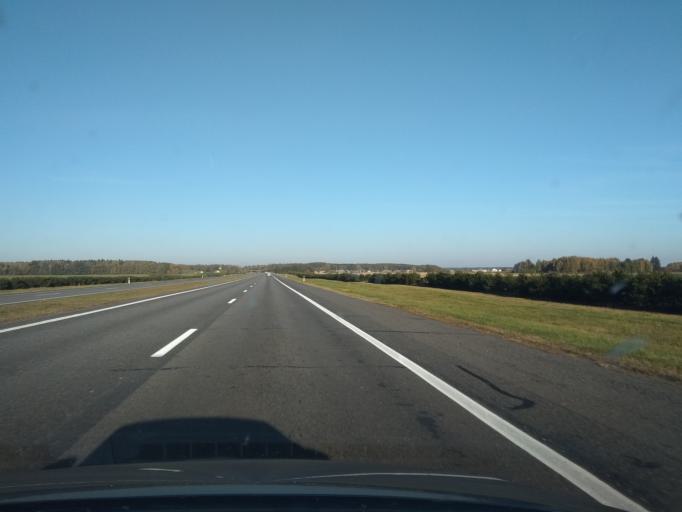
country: BY
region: Brest
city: Ivatsevichy
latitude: 52.6692
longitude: 25.3017
